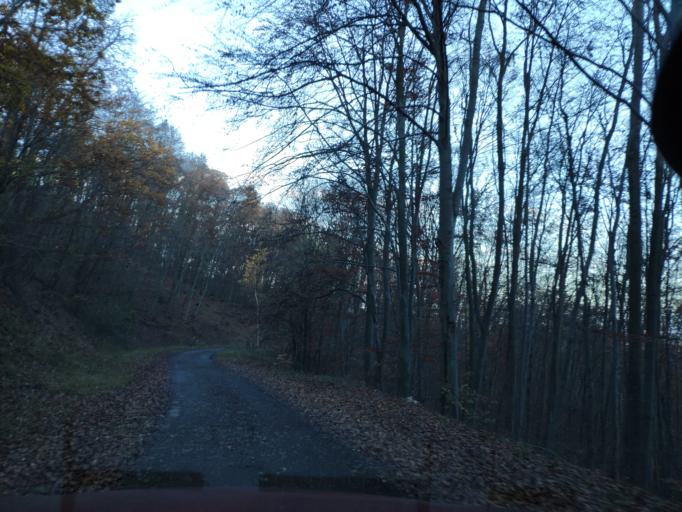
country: SK
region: Kosicky
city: Secovce
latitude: 48.5910
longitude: 21.5088
